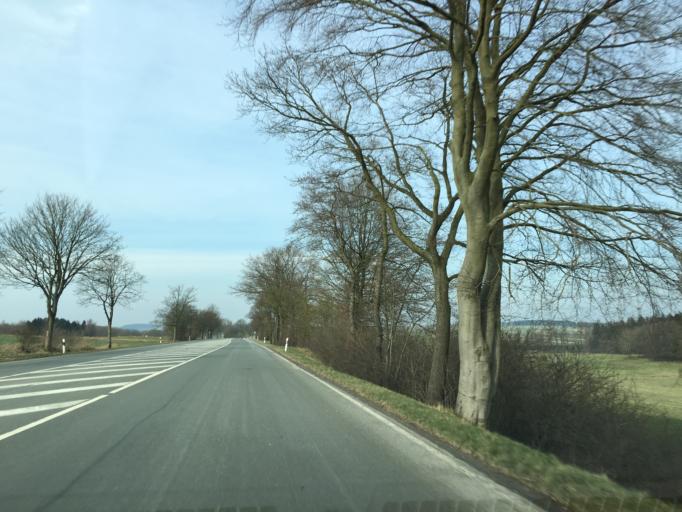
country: DE
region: North Rhine-Westphalia
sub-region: Regierungsbezirk Detmold
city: Willebadessen
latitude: 51.5738
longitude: 8.9997
